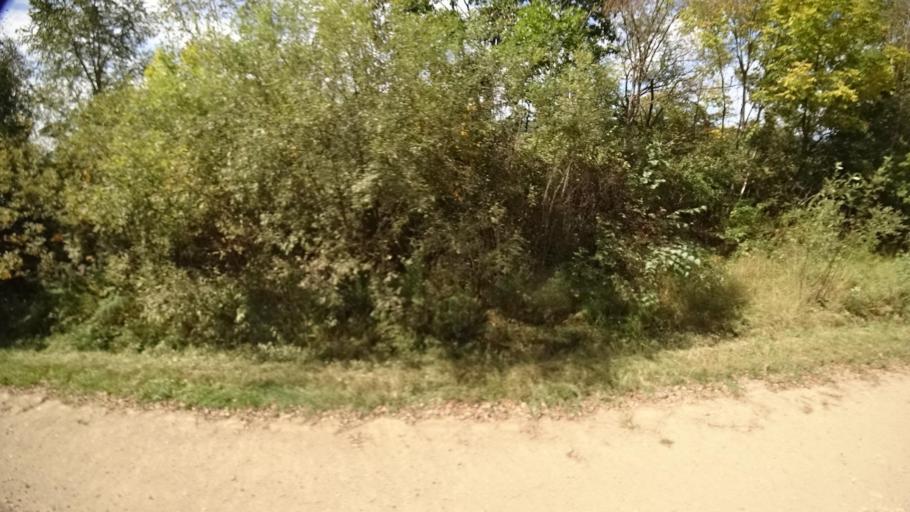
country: RU
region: Primorskiy
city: Yakovlevka
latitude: 44.6860
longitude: 133.6180
